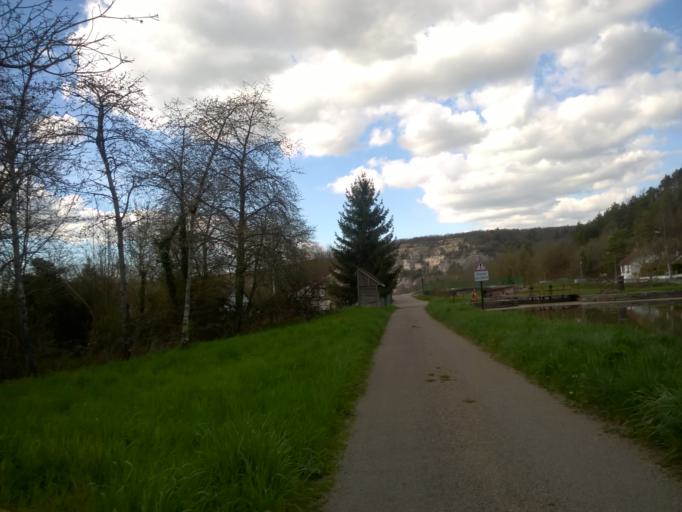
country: FR
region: Bourgogne
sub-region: Departement de l'Yonne
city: Ravieres
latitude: 47.7058
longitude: 4.2445
